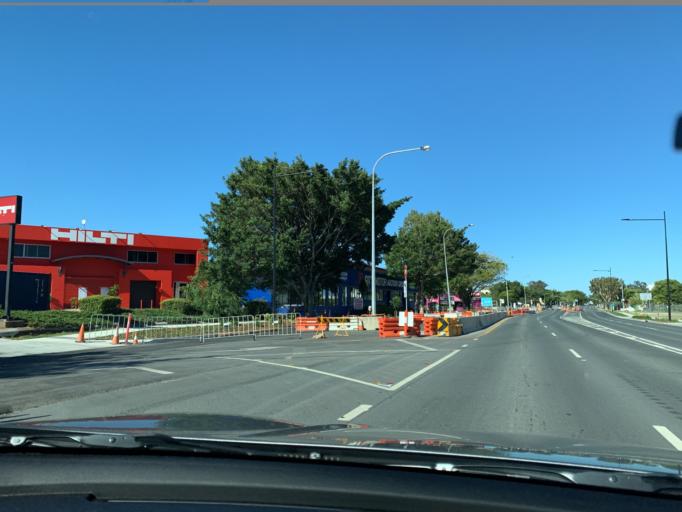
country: AU
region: Queensland
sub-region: Brisbane
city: Ascot
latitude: -27.4353
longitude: 153.0765
